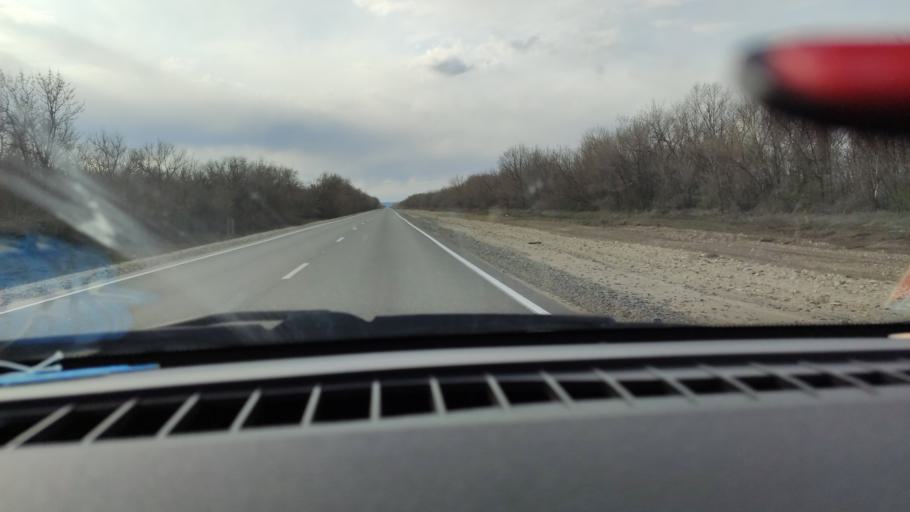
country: RU
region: Saratov
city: Privolzhskiy
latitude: 51.1654
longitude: 45.9478
